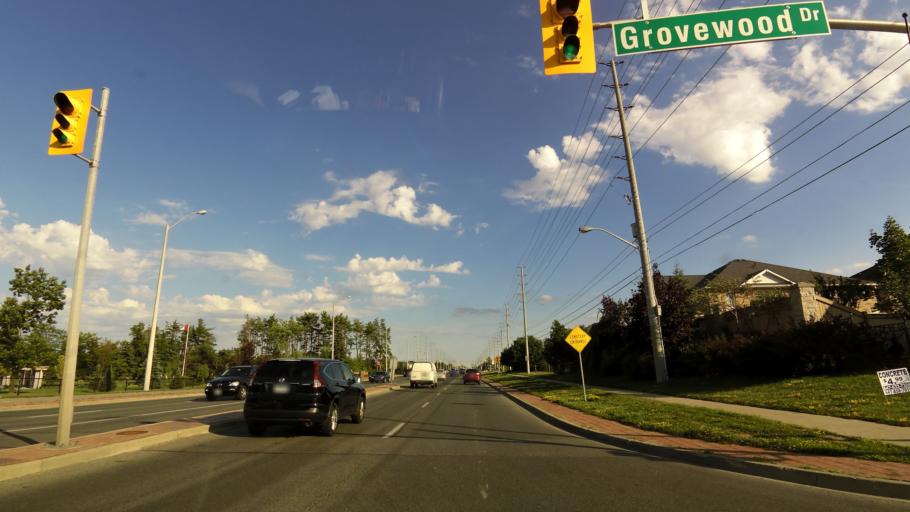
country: CA
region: Ontario
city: Brampton
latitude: 43.6881
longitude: -79.8112
